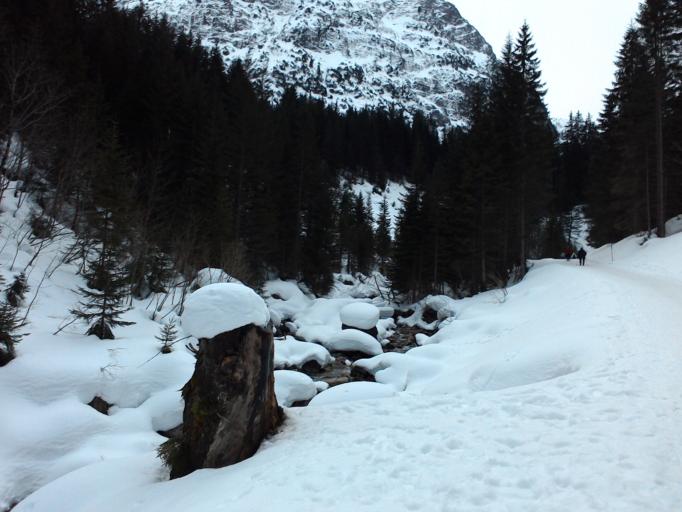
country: AT
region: Vorarlberg
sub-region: Politischer Bezirk Bregenz
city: Mittelberg
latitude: 47.2983
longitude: 10.1170
